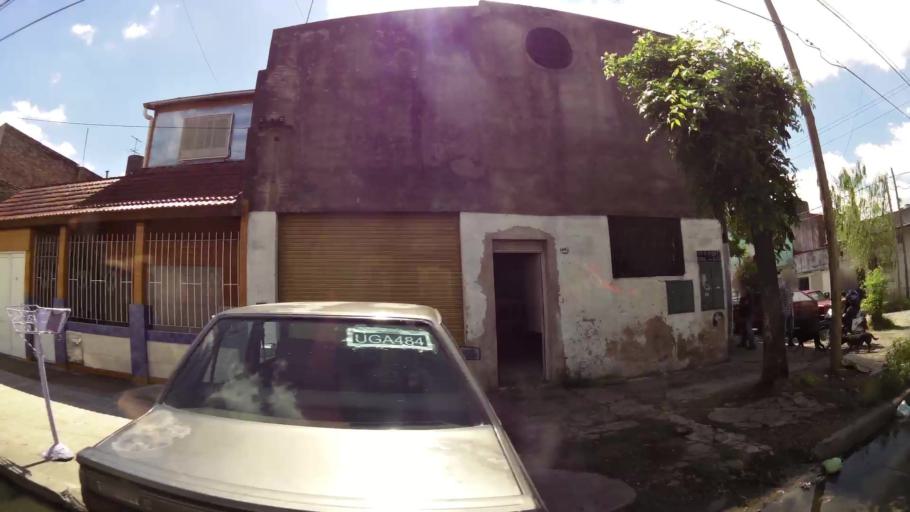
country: AR
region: Buenos Aires
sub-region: Partido de Lanus
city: Lanus
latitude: -34.6724
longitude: -58.4274
